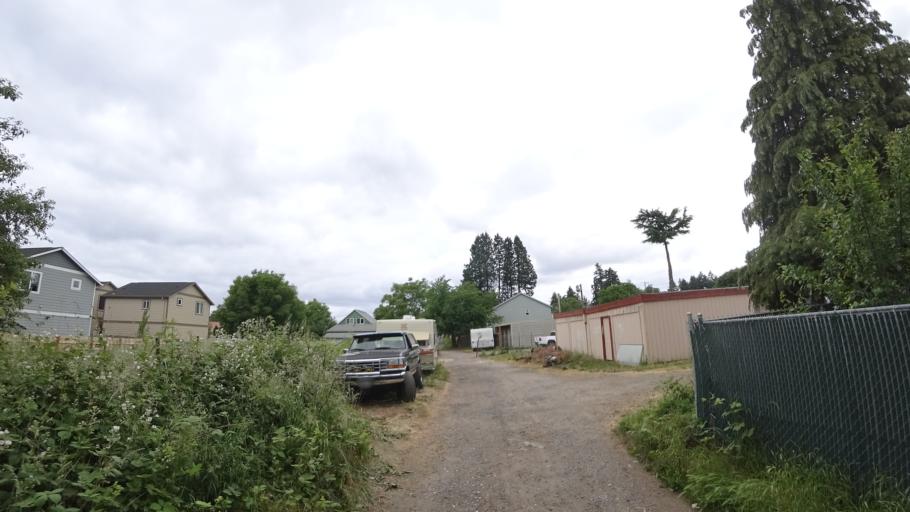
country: US
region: Oregon
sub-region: Multnomah County
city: Lents
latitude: 45.4828
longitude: -122.5742
